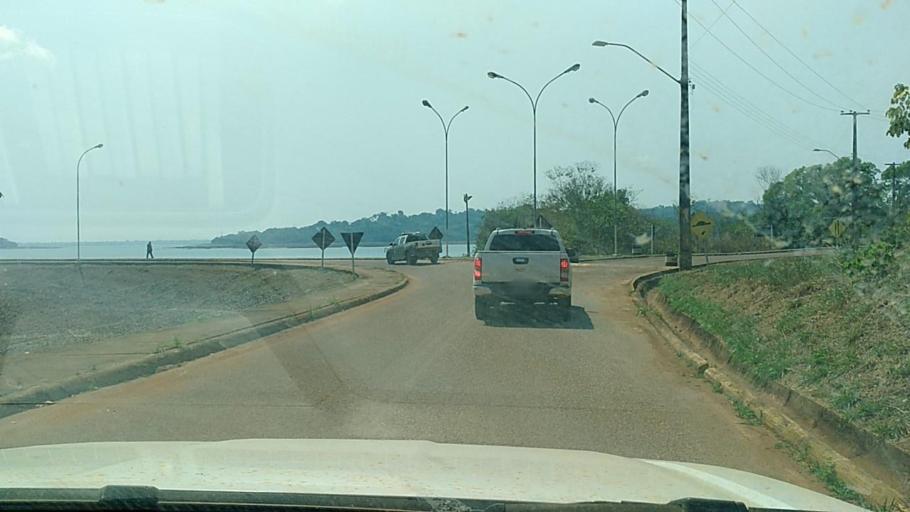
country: BR
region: Rondonia
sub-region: Porto Velho
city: Porto Velho
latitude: -8.7531
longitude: -63.4580
